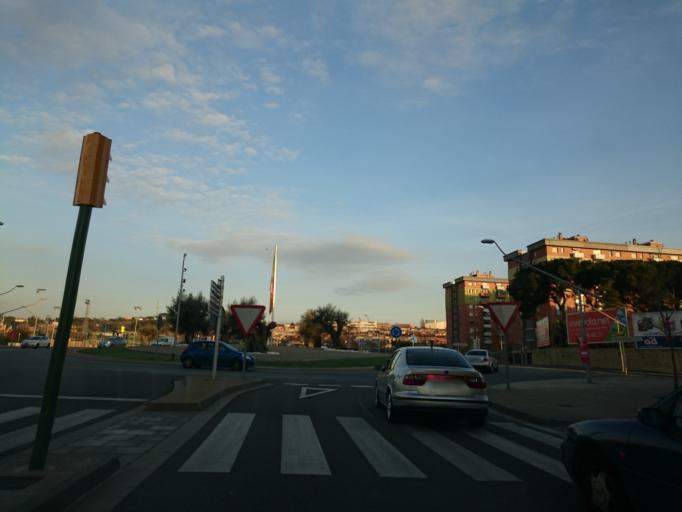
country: ES
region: Catalonia
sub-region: Provincia de Barcelona
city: Les Franqueses del Valles
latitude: 41.6227
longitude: 2.2931
